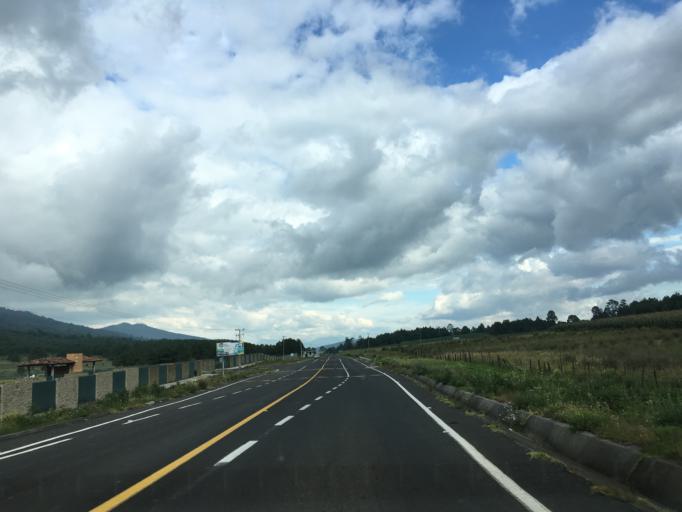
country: MX
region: Michoacan
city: Pichataro
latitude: 19.6057
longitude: -101.8465
